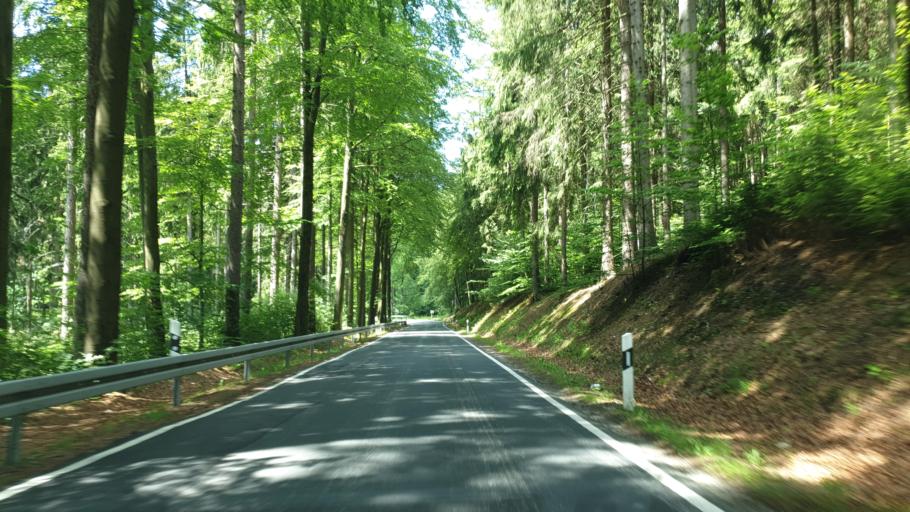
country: DE
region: Saxony
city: Lauter
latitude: 50.5160
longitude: 12.7413
